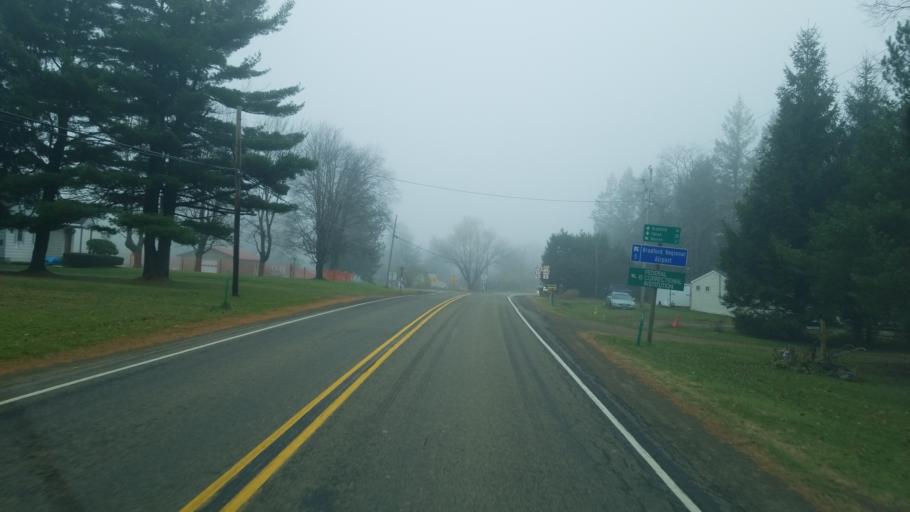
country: US
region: Pennsylvania
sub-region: McKean County
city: Smethport
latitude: 41.8087
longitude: -78.5398
